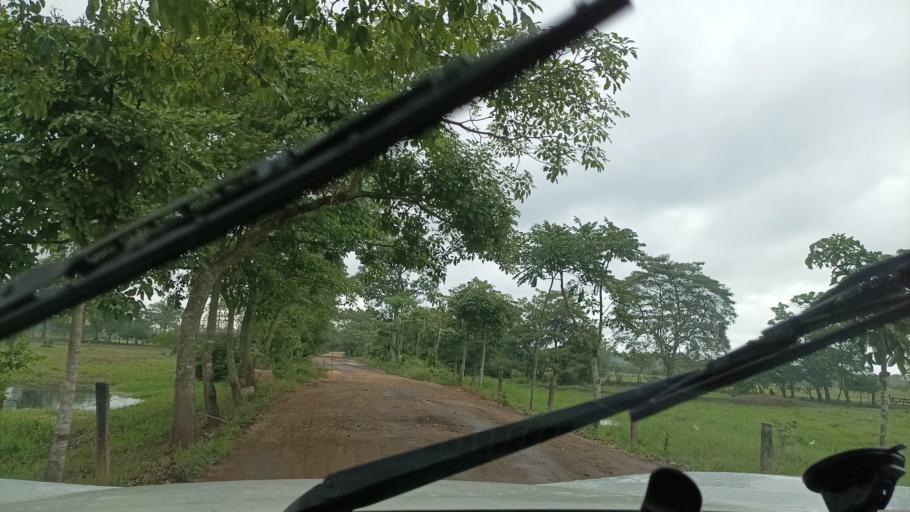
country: MX
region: Veracruz
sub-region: Moloacan
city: Cuichapa
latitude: 17.7761
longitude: -94.3880
